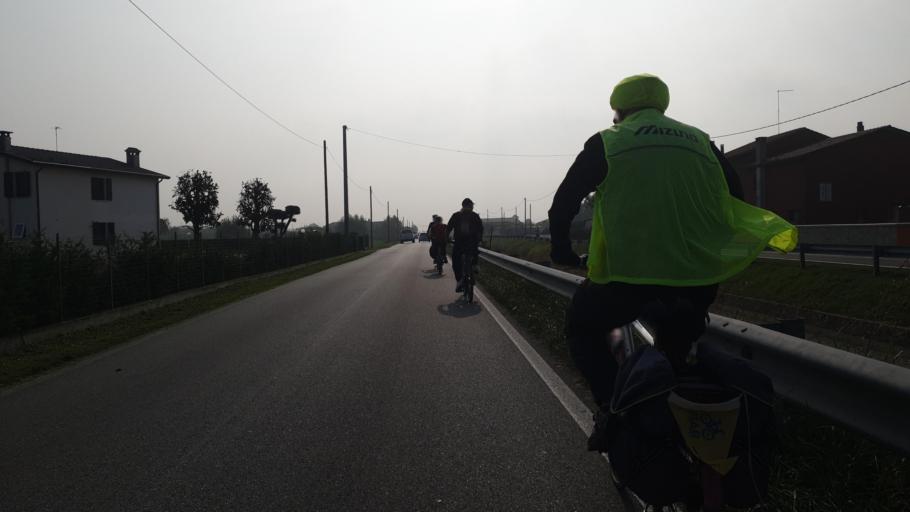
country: IT
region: Veneto
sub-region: Provincia di Padova
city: Corte
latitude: 45.3015
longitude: 12.0782
